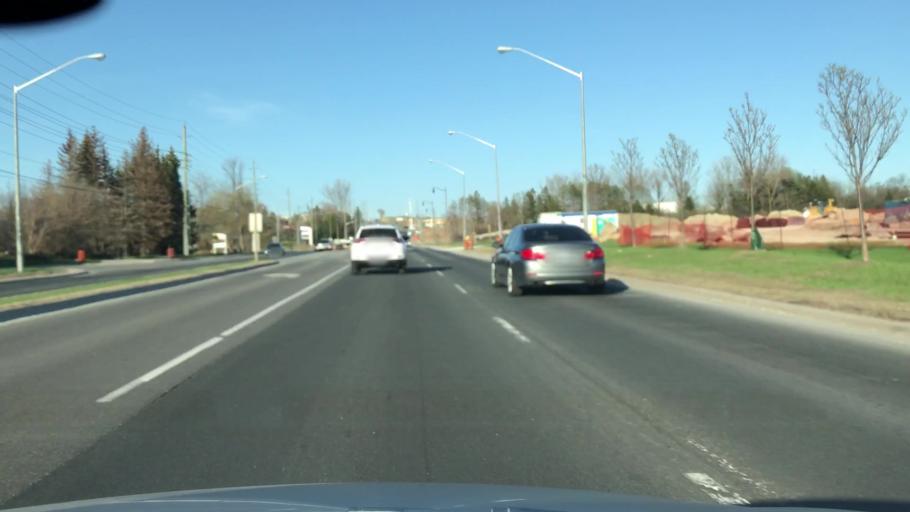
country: CA
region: Ontario
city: Newmarket
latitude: 44.0091
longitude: -79.4261
